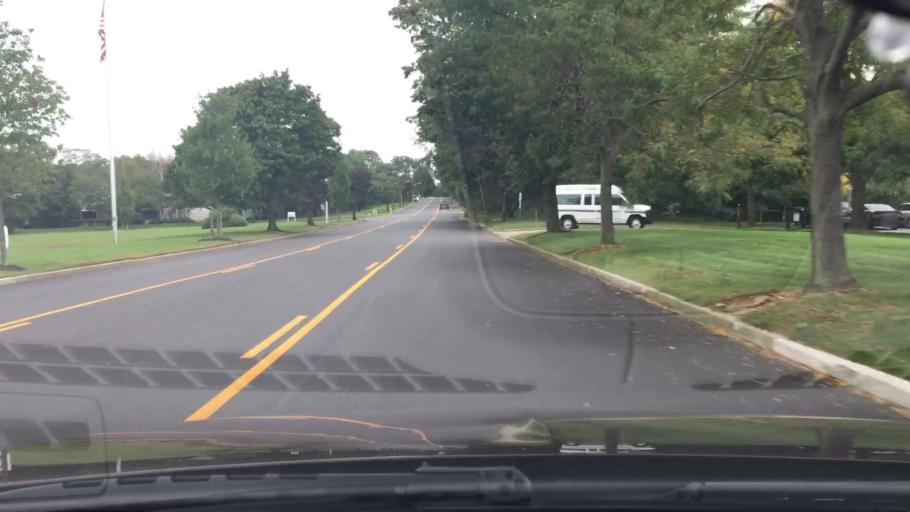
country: US
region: New York
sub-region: Suffolk County
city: Brentwood
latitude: 40.8109
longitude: -73.2449
